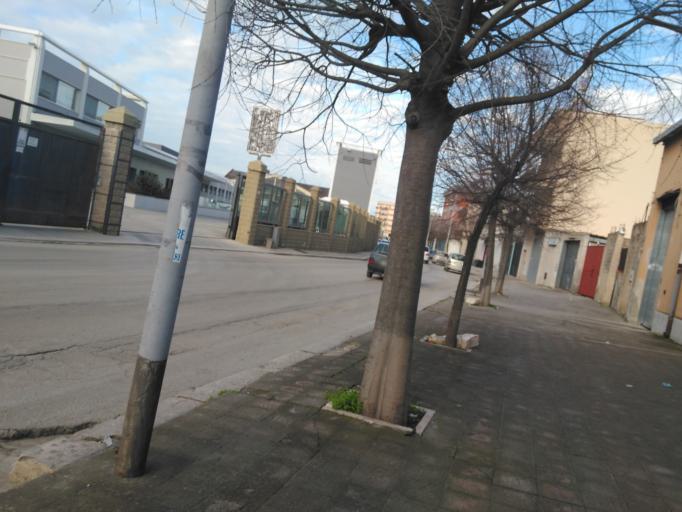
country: IT
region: Apulia
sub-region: Provincia di Barletta - Andria - Trani
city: Andria
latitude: 41.2179
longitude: 16.2962
